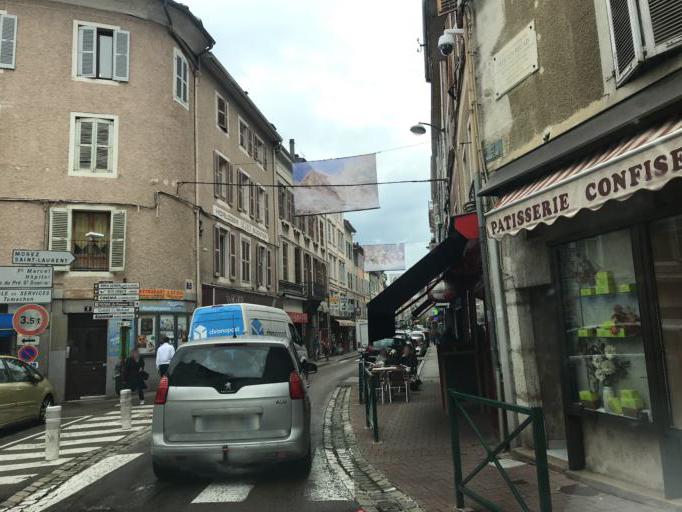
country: FR
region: Franche-Comte
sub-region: Departement du Jura
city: Saint-Claude
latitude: 46.3876
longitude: 5.8642
